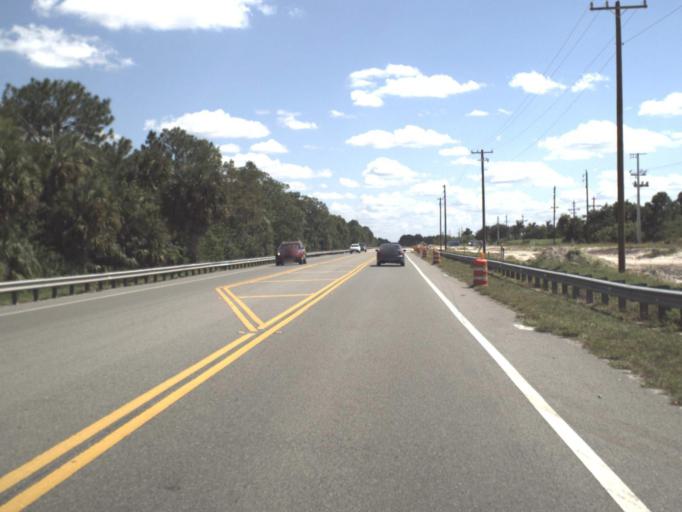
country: US
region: Florida
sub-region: Collier County
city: Lely Resort
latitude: 26.0374
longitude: -81.6586
